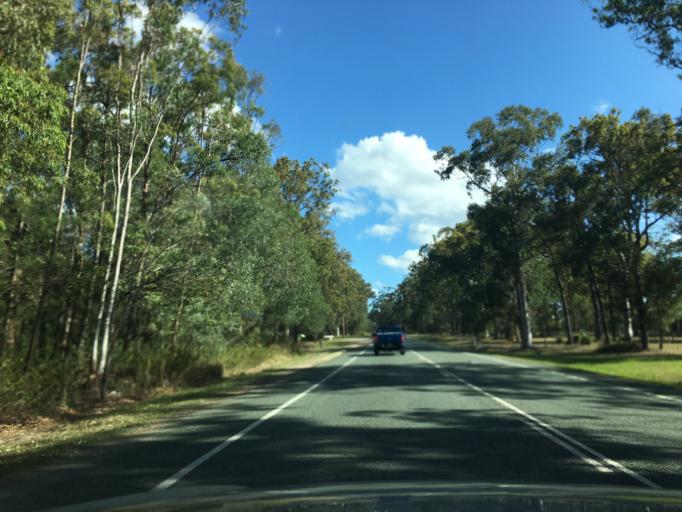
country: AU
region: Queensland
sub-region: Logan
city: Chambers Flat
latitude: -27.7903
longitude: 153.1001
